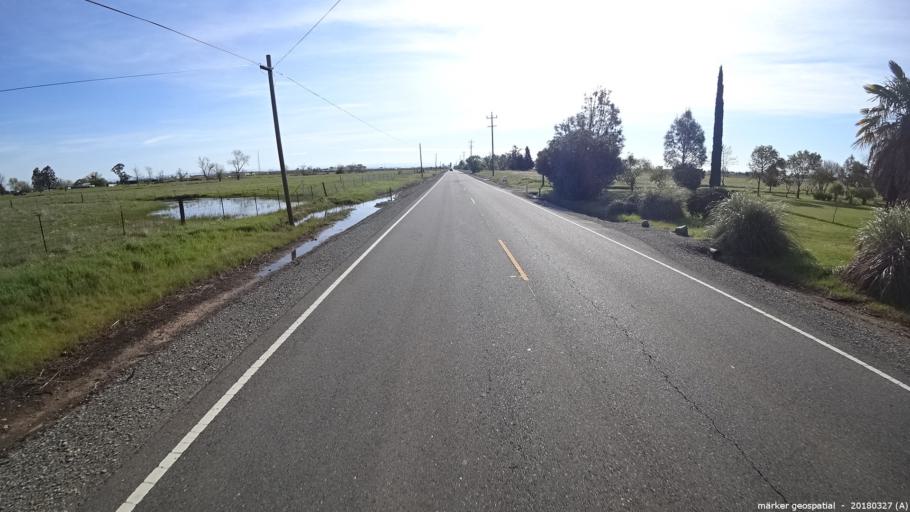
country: US
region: California
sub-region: Sacramento County
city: Vineyard
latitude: 38.4964
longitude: -121.3238
